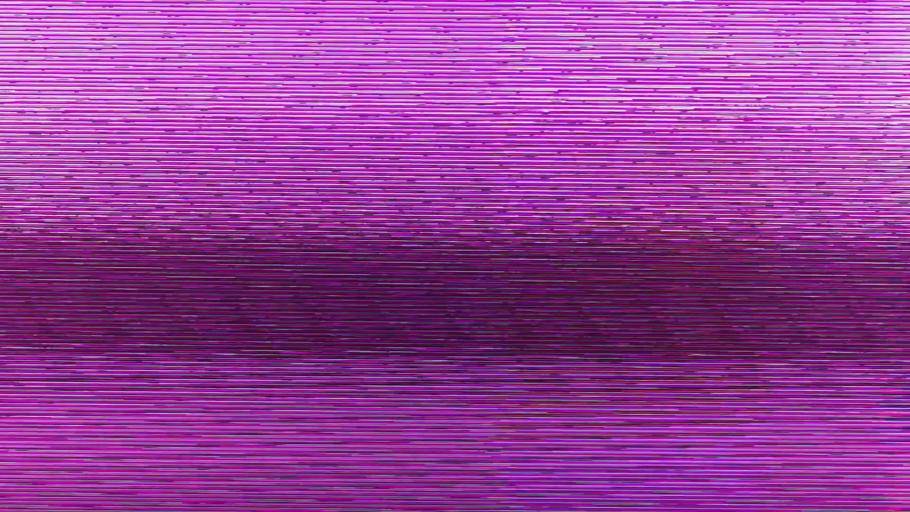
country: US
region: Michigan
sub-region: Oakland County
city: Sylvan Lake
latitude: 42.6277
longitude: -83.3188
